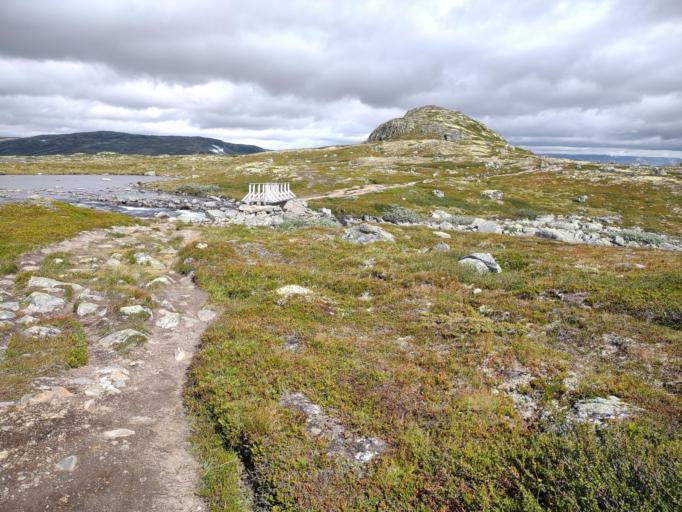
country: NO
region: Buskerud
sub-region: Hol
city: Geilo
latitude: 60.4495
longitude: 7.7016
